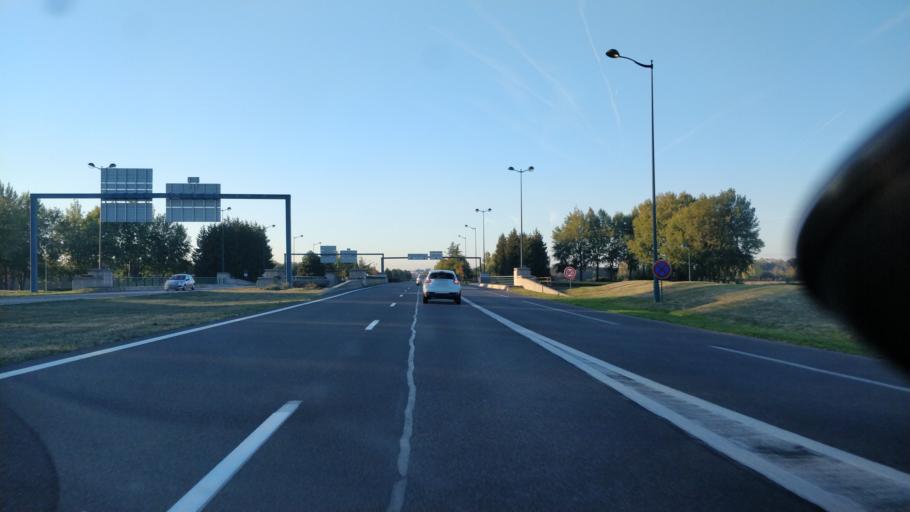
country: FR
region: Ile-de-France
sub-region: Departement de Seine-et-Marne
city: Magny-le-Hongre
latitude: 48.8540
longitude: 2.8013
